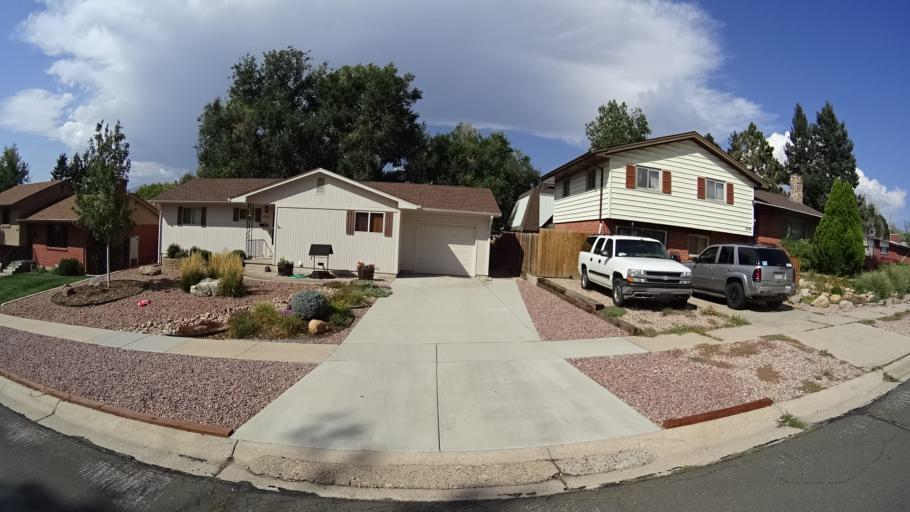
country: US
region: Colorado
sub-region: El Paso County
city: Colorado Springs
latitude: 38.8648
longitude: -104.7713
